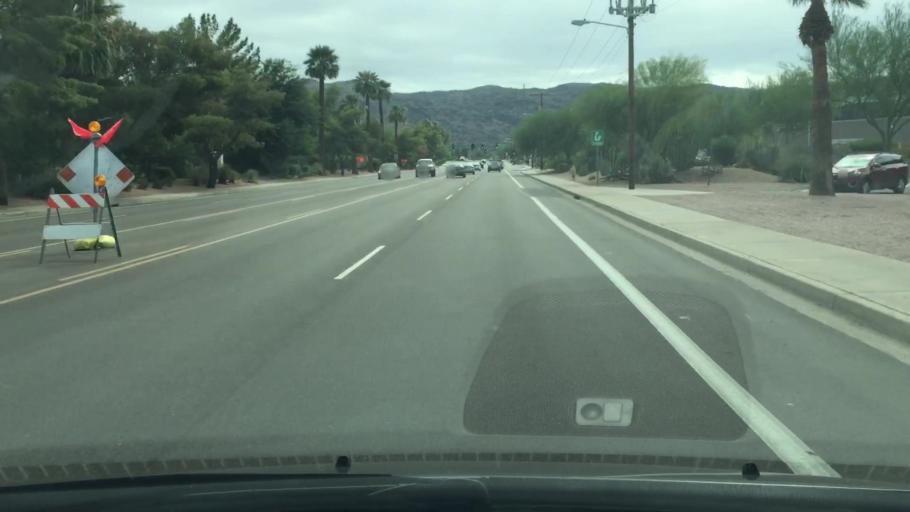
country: US
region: Arizona
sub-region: Maricopa County
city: Guadalupe
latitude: 33.3841
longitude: -112.0303
